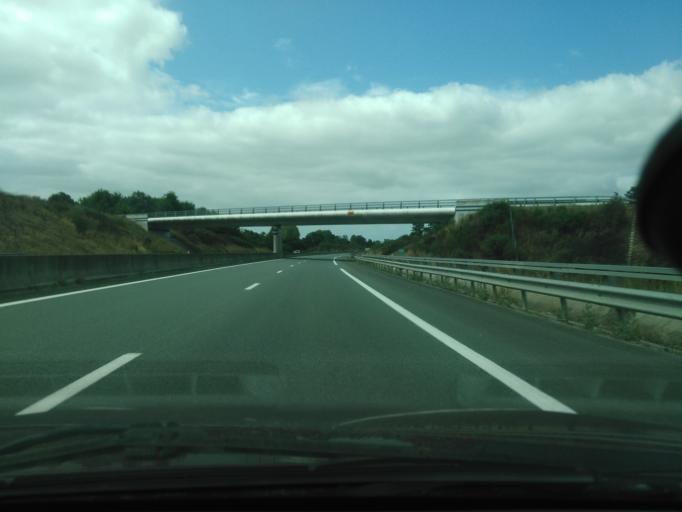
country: FR
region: Pays de la Loire
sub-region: Departement de la Vendee
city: Nesmy
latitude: 46.6319
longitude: -1.4048
